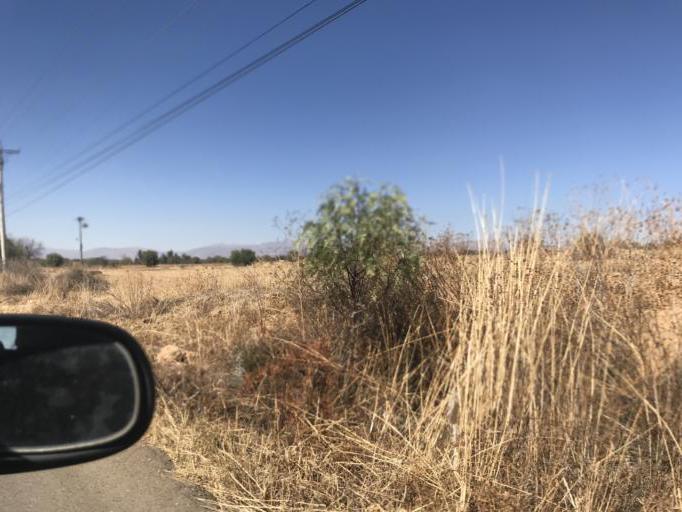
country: BO
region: Cochabamba
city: Tarata
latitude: -17.6066
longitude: -65.9975
